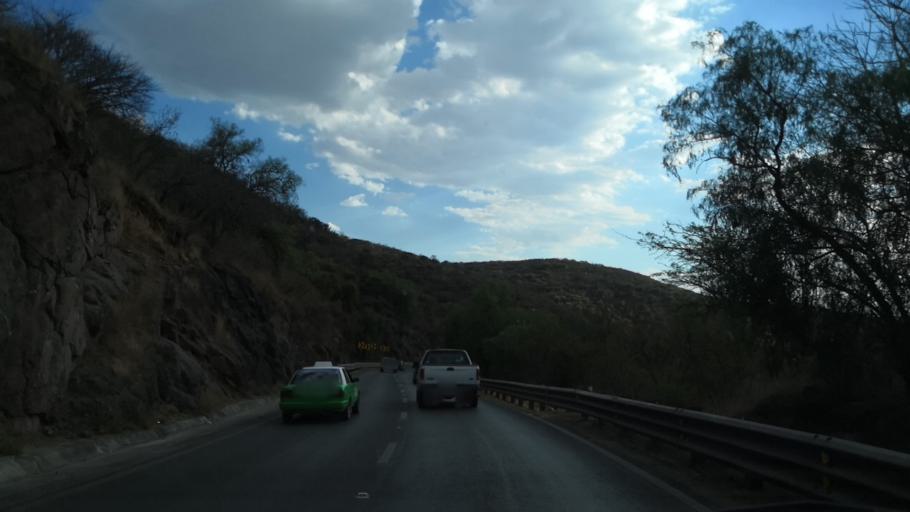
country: MX
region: Guanajuato
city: Marfil
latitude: 21.0073
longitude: -101.2742
